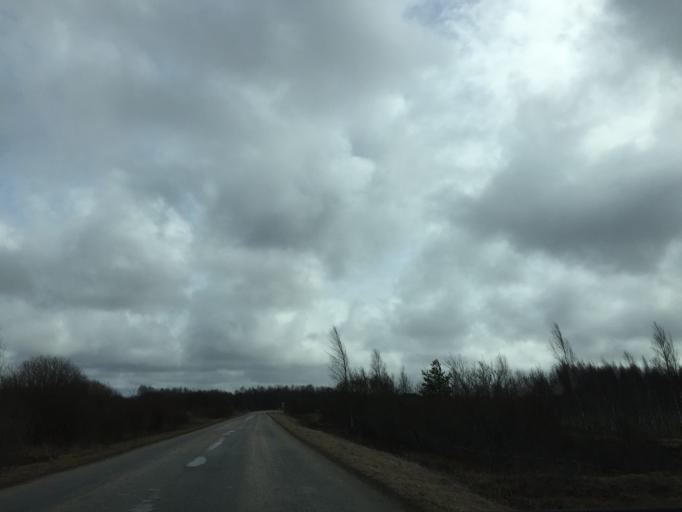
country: EE
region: Laeaene
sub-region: Lihula vald
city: Lihula
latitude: 58.7262
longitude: 23.9123
